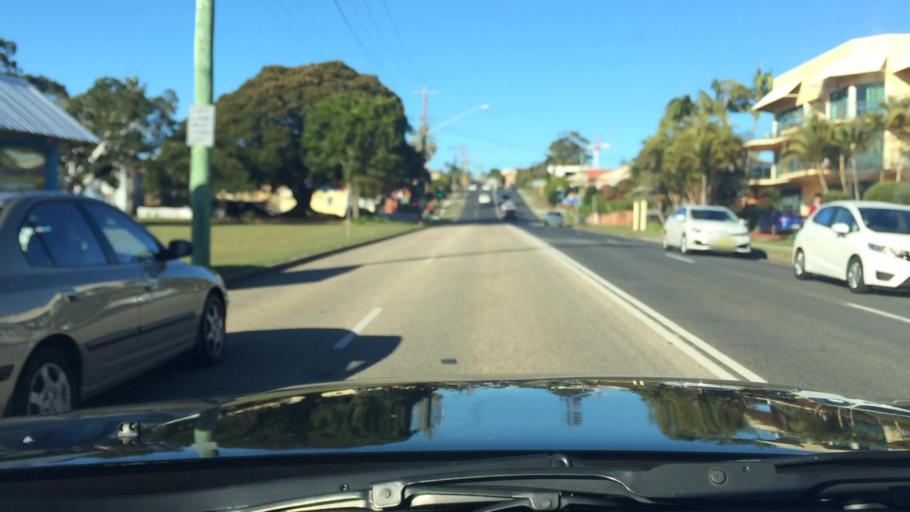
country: AU
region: New South Wales
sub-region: Port Macquarie-Hastings
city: Port Macquarie
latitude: -31.4305
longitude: 152.8998
